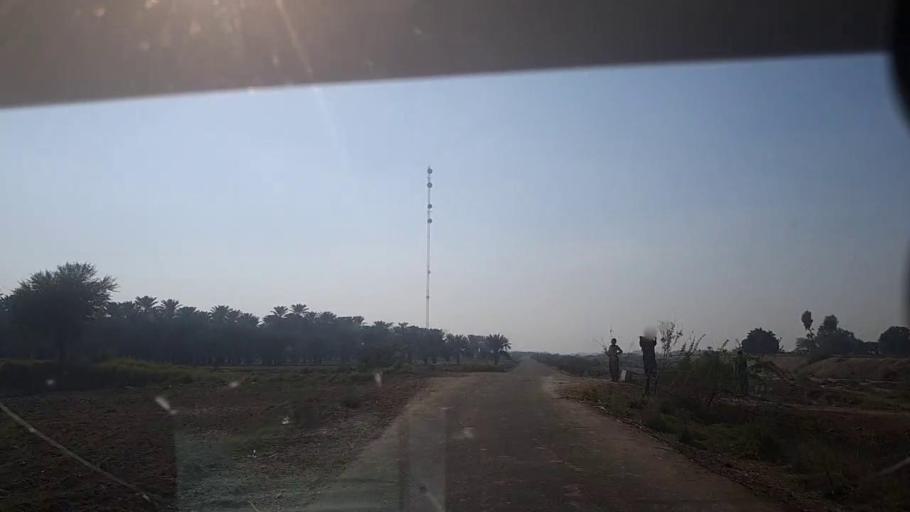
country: PK
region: Sindh
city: Gambat
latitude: 27.3861
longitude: 68.5916
